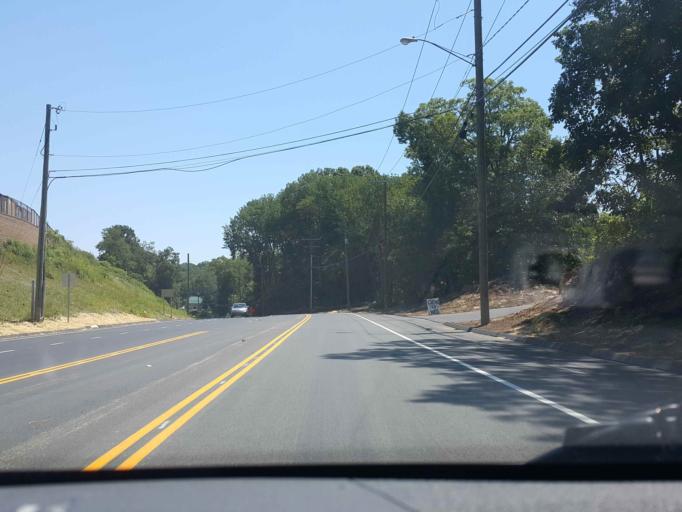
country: US
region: Connecticut
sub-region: New Haven County
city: Guilford
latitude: 41.3008
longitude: -72.7088
